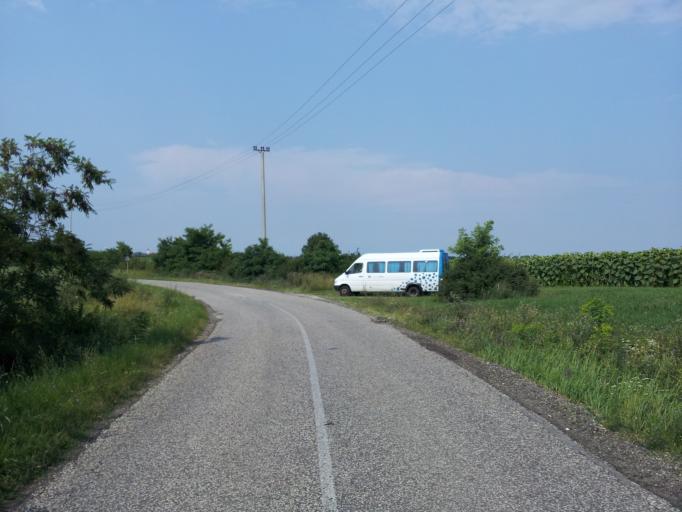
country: HU
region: Pest
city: Szigetujfalu
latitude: 47.2175
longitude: 18.9214
